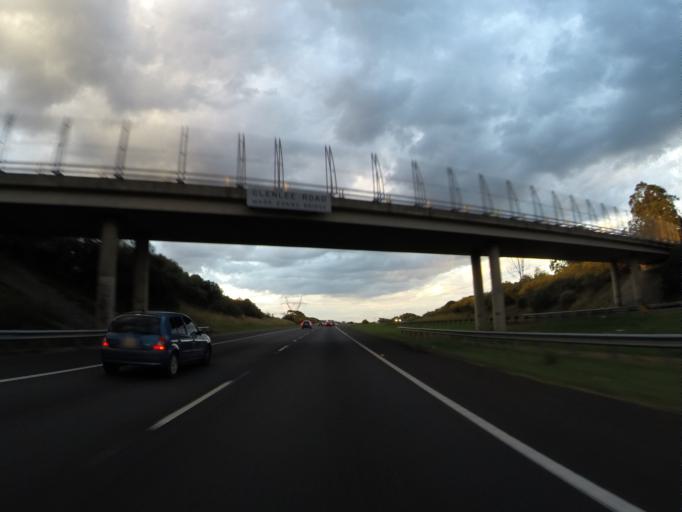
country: AU
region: New South Wales
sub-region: Campbelltown Municipality
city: Glen Alpine
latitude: -34.0880
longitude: 150.7682
